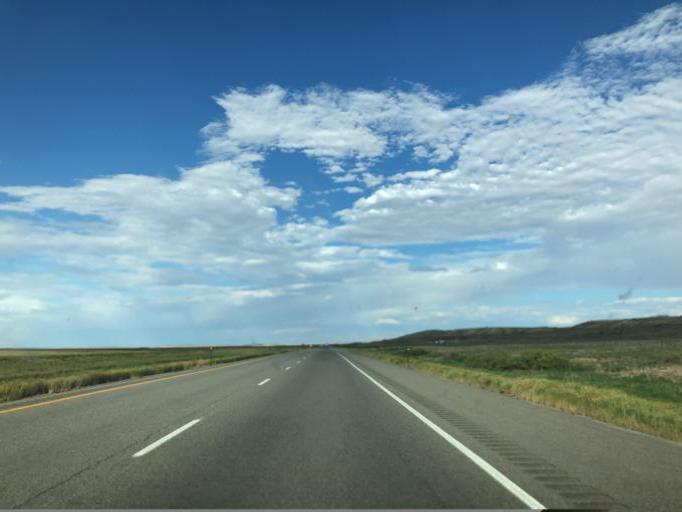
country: US
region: Wyoming
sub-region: Carbon County
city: Rawlins
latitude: 41.6417
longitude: -108.1940
